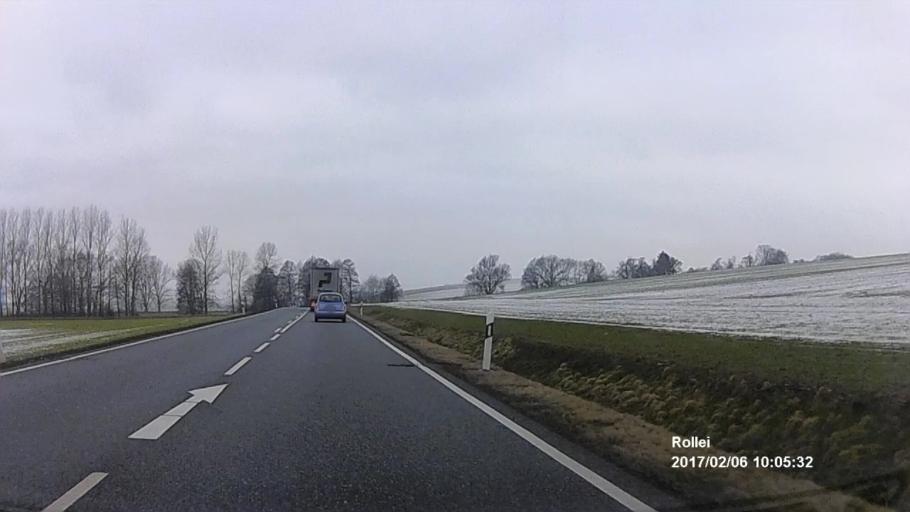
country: DE
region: Thuringia
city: Etzelsrode
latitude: 51.5321
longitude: 10.6156
